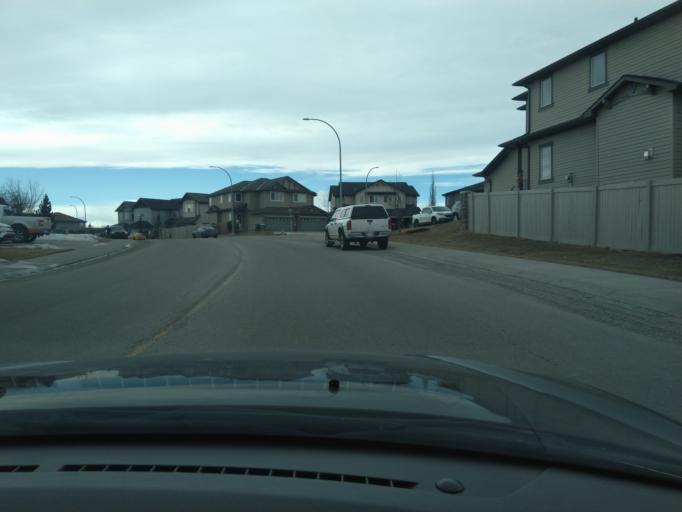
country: CA
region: Alberta
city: Calgary
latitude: 51.1655
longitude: -114.0993
